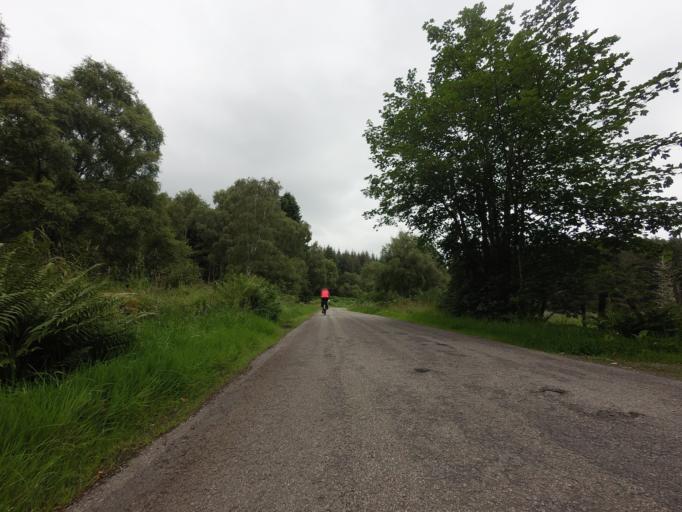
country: GB
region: Scotland
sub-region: Highland
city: Evanton
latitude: 57.8883
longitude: -4.3878
